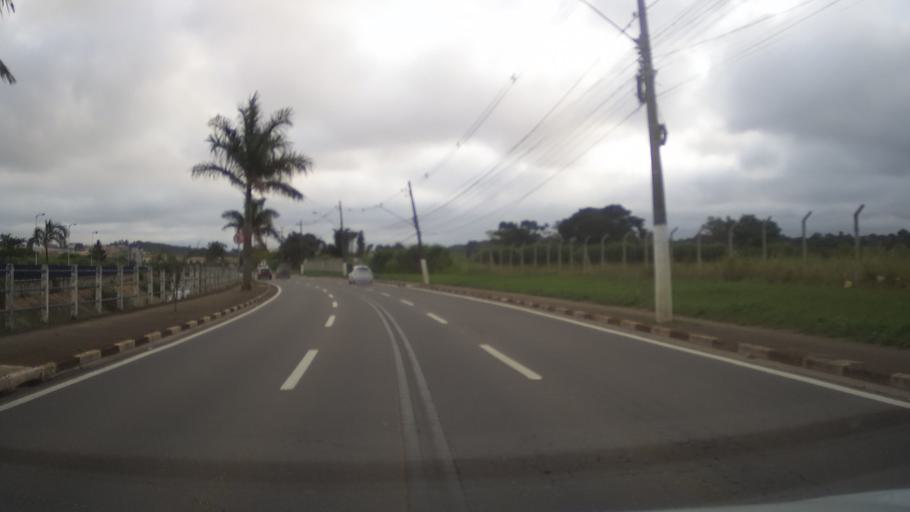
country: BR
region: Sao Paulo
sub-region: Aruja
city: Aruja
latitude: -23.4039
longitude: -46.3644
